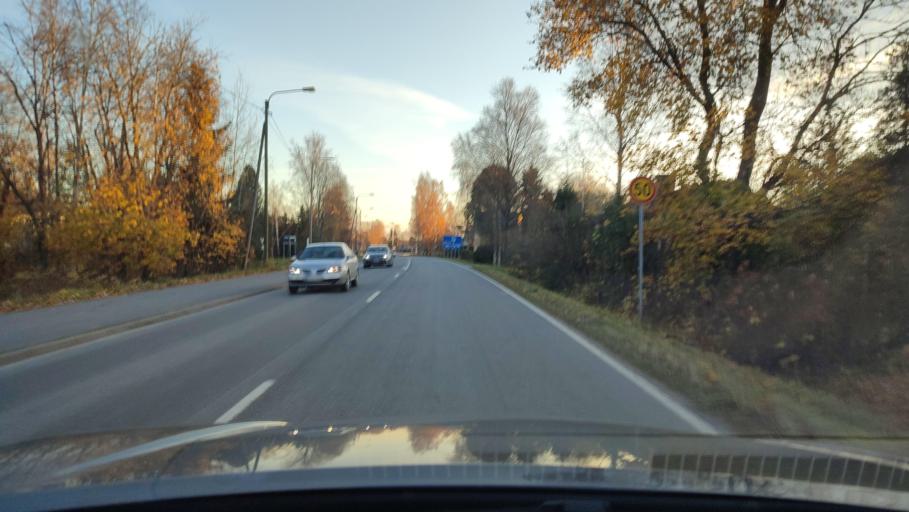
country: FI
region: Ostrobothnia
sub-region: Sydosterbotten
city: Naerpes
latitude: 62.4857
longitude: 21.3388
